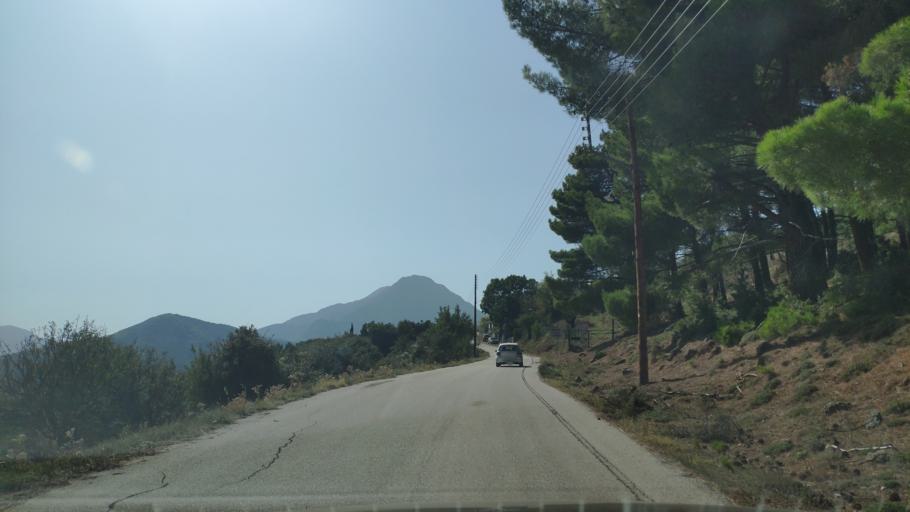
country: GR
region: West Greece
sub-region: Nomos Achaias
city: Aiyira
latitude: 37.9527
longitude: 22.3333
